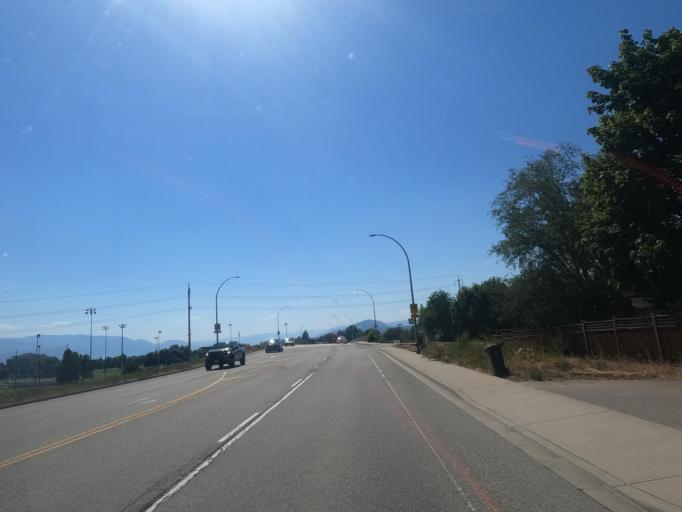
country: CA
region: British Columbia
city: Kelowna
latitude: 49.8885
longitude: -119.4560
